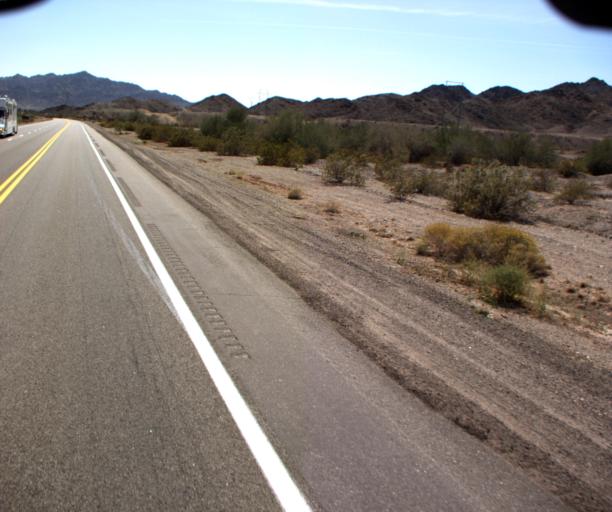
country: US
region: Arizona
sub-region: Yuma County
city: Fortuna Foothills
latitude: 32.7965
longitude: -114.3812
